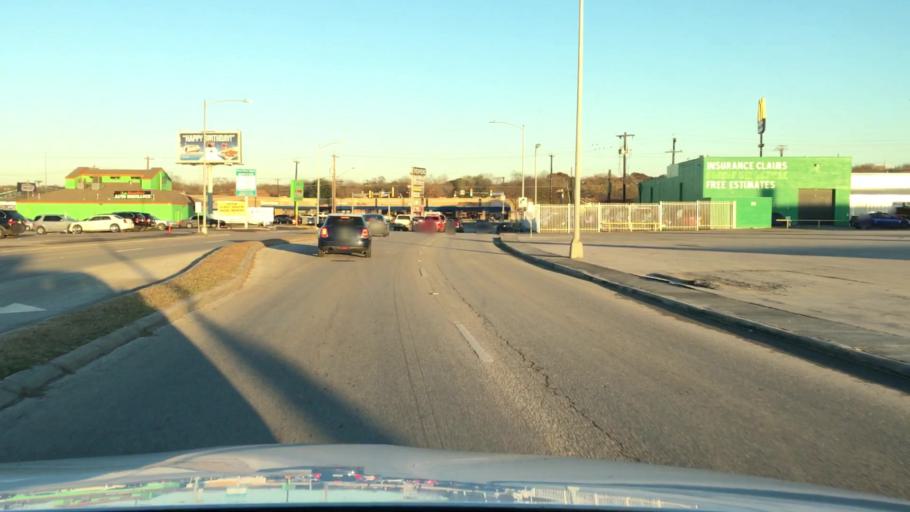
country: US
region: Texas
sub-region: Bexar County
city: Windcrest
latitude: 29.5445
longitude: -98.4125
